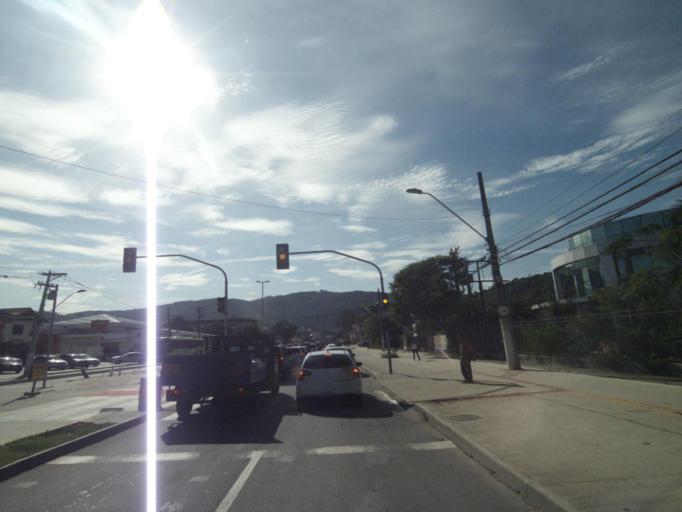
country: BR
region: Rio de Janeiro
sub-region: Niteroi
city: Niteroi
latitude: -22.9371
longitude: -43.0618
